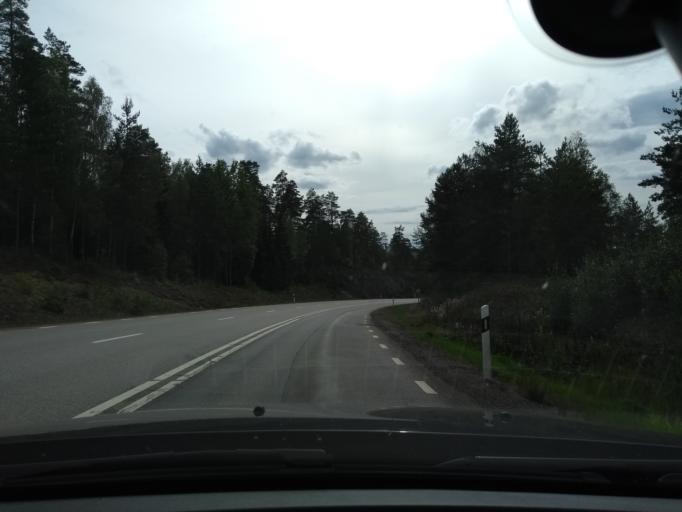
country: SE
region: Joenkoeping
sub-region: Eksjo Kommun
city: Mariannelund
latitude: 57.6278
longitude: 15.6180
